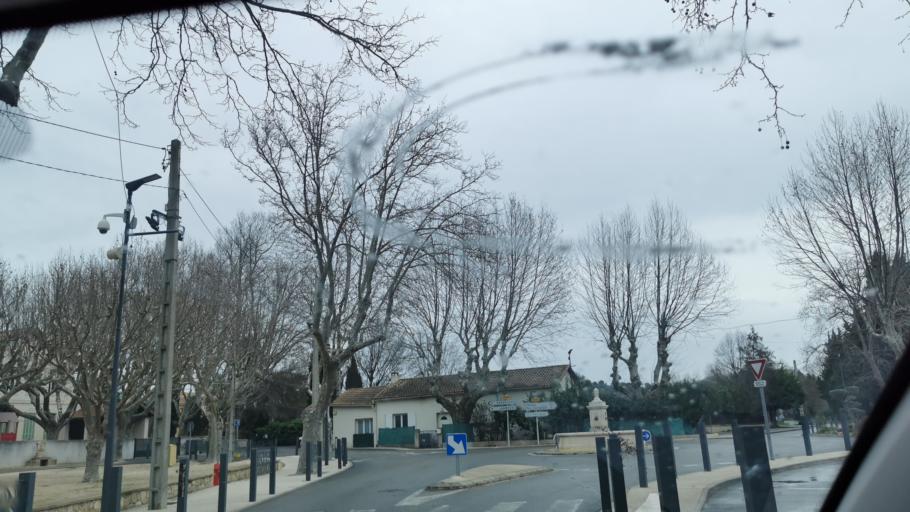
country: FR
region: Provence-Alpes-Cote d'Azur
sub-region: Departement des Bouches-du-Rhone
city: Pelissanne
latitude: 43.6300
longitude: 5.1764
